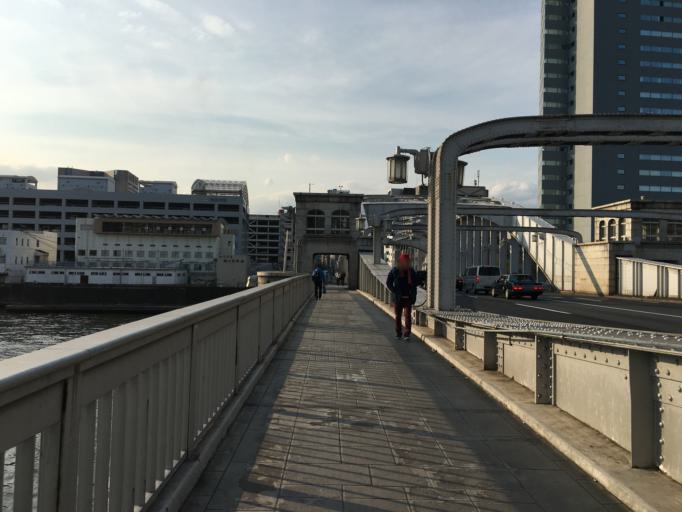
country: JP
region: Tokyo
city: Tokyo
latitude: 35.6621
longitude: 139.7749
